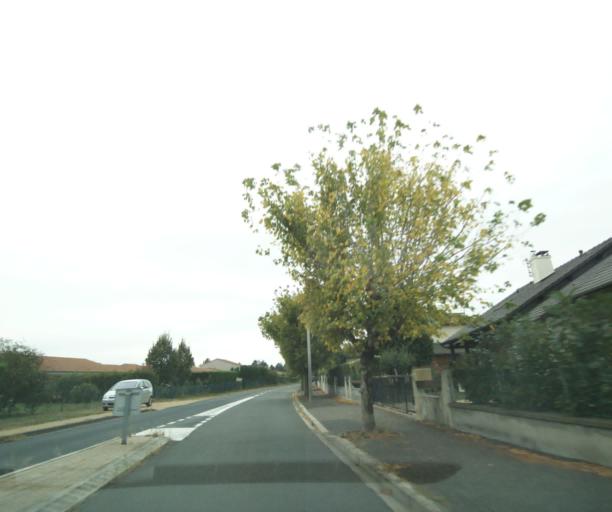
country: FR
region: Auvergne
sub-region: Departement du Puy-de-Dome
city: Gerzat
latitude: 45.8368
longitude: 3.1497
